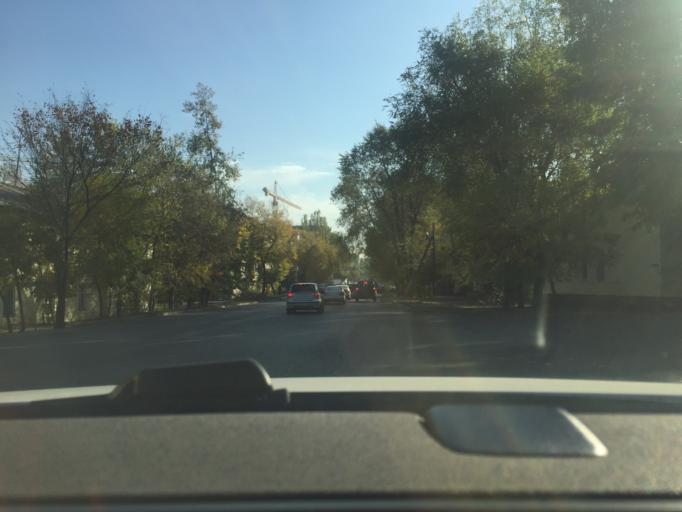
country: KZ
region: Almaty Qalasy
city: Almaty
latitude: 43.2457
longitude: 76.9130
